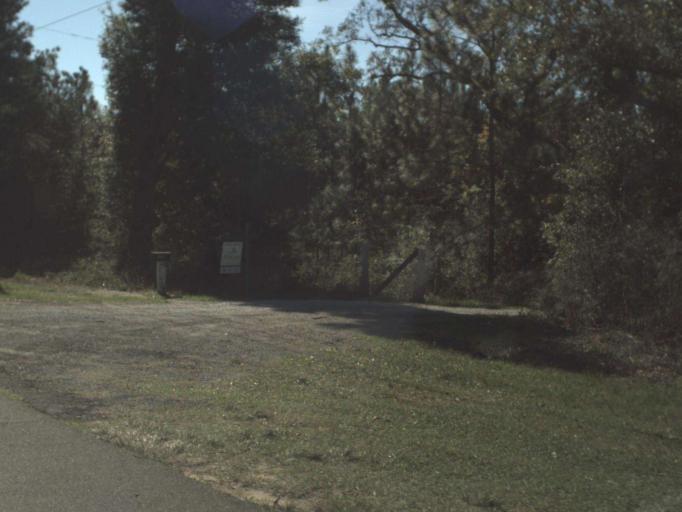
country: US
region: Florida
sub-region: Okaloosa County
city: Crestview
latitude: 30.8530
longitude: -86.6750
